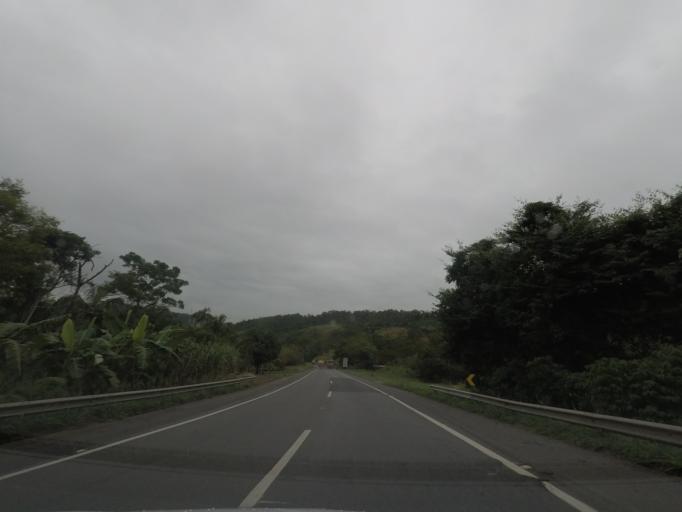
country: BR
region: Sao Paulo
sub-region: Cajati
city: Cajati
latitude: -24.7895
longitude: -48.2044
